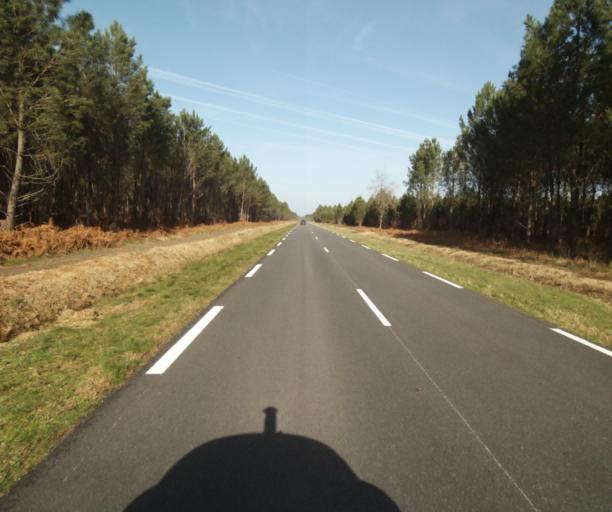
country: FR
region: Aquitaine
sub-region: Departement de la Gironde
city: Grignols
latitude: 44.1849
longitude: -0.0929
